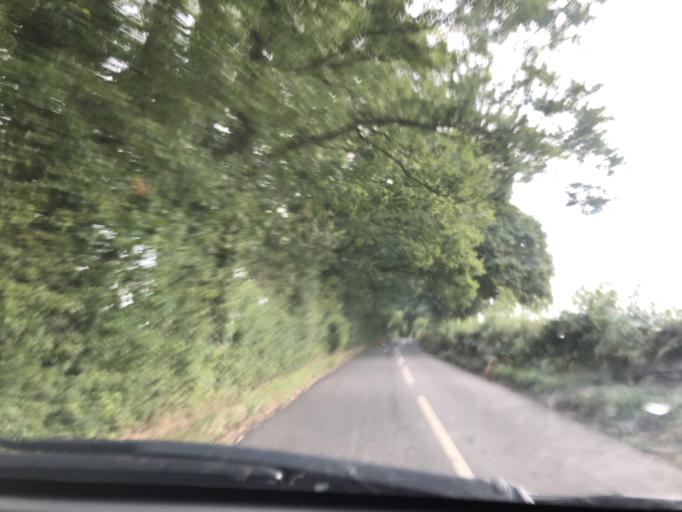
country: GB
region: England
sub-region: Kent
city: Westerham
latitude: 51.2329
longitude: 0.0887
